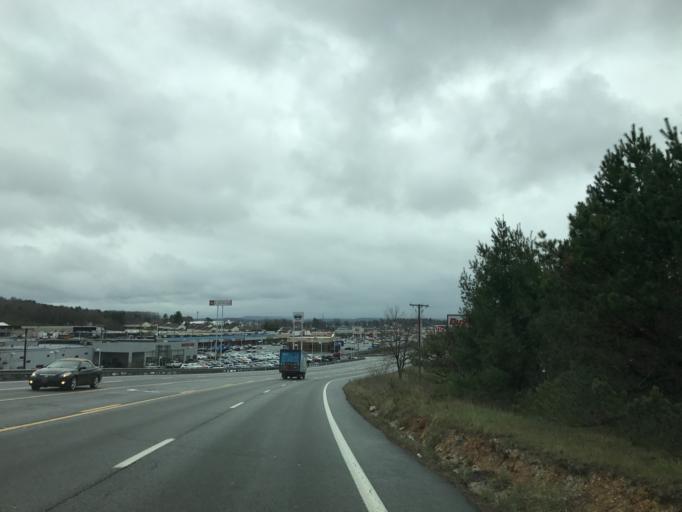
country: US
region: West Virginia
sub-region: Raleigh County
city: Prosperity
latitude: 37.8168
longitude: -81.1869
